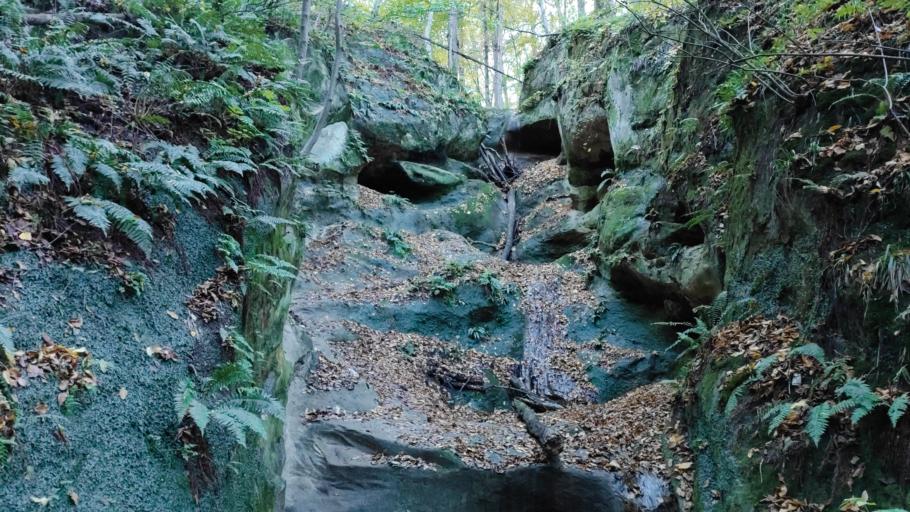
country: RU
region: Krasnodarskiy
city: Goryachiy Klyuch
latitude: 44.5932
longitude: 39.1236
